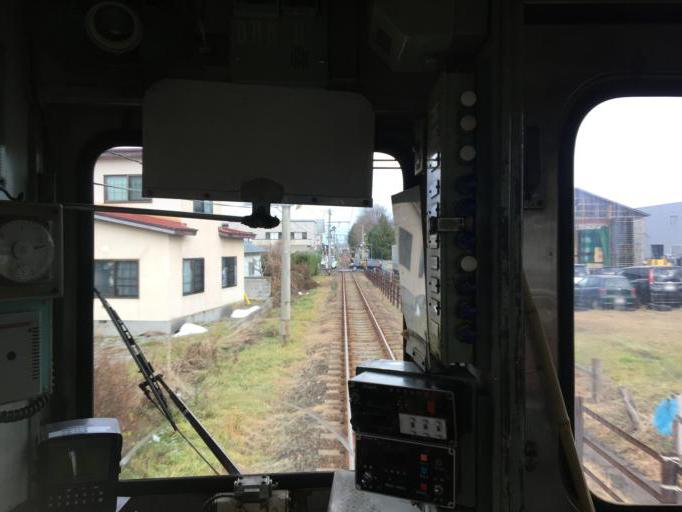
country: JP
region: Aomori
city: Hirosaki
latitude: 40.5761
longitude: 140.4730
